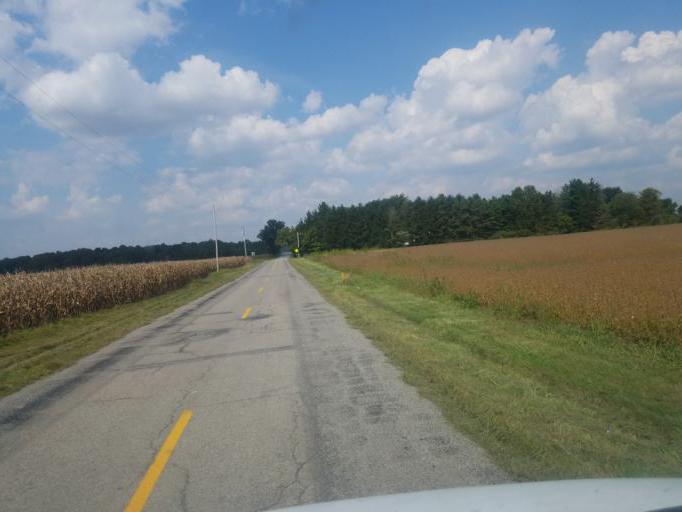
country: US
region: Ohio
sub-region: Hardin County
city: Ada
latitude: 40.6436
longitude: -83.8863
